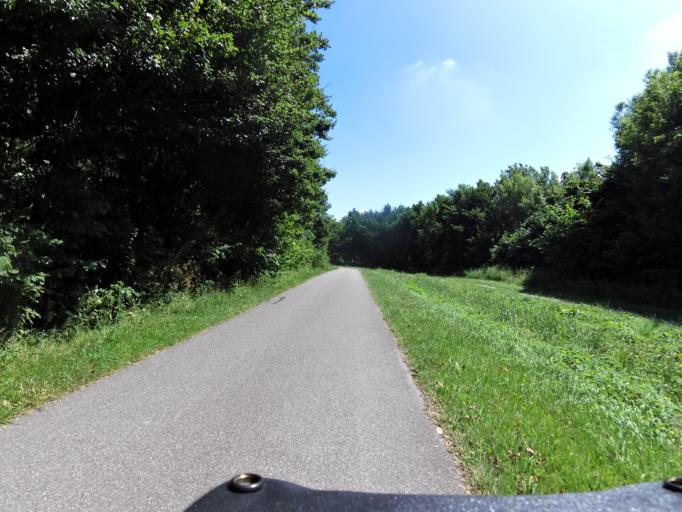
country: NL
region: South Holland
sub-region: Gemeente Delft
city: Delft
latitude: 51.9786
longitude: 4.3621
